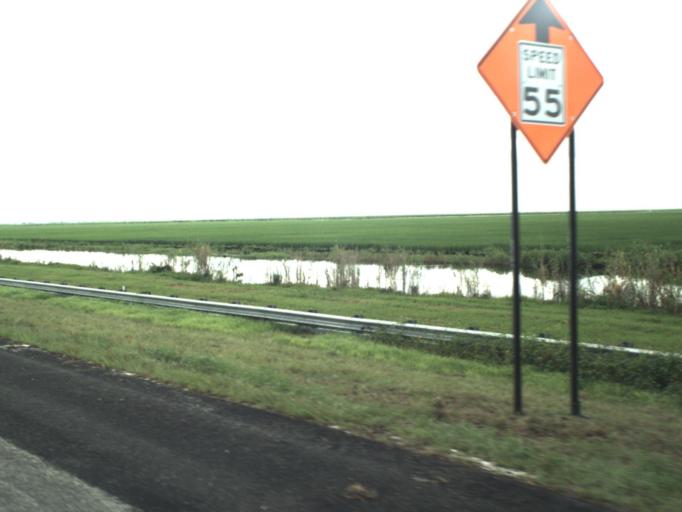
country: US
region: Florida
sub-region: Palm Beach County
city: Loxahatchee Groves
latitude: 26.7254
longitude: -80.4638
